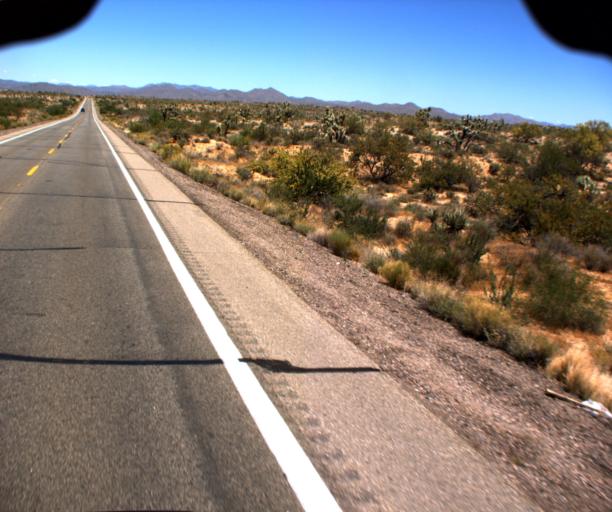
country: US
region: Arizona
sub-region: Yavapai County
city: Bagdad
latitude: 34.3258
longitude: -113.1391
